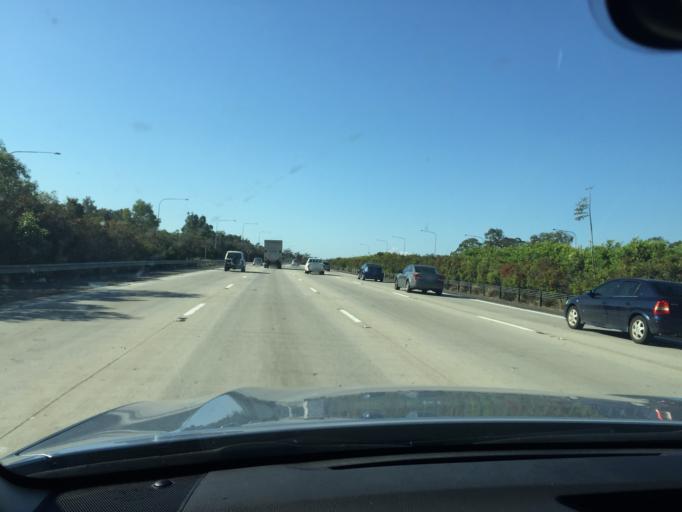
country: AU
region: Queensland
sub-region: Gold Coast
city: Yatala
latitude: -27.7360
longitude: 153.2288
